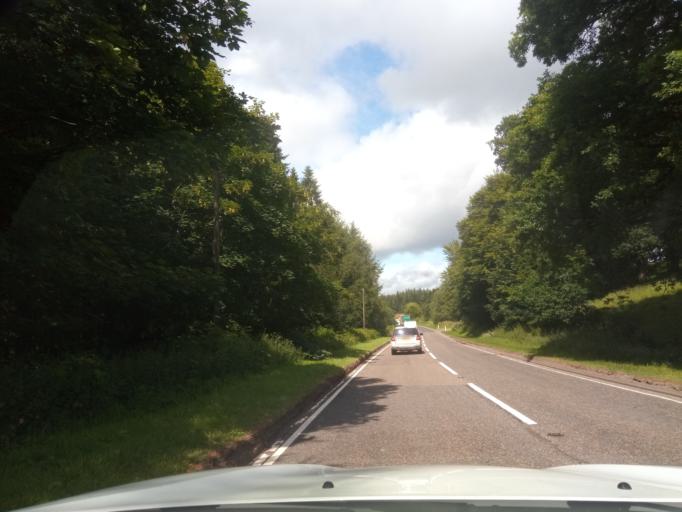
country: GB
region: Scotland
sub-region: Stirling
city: Callander
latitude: 56.2194
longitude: -4.1629
